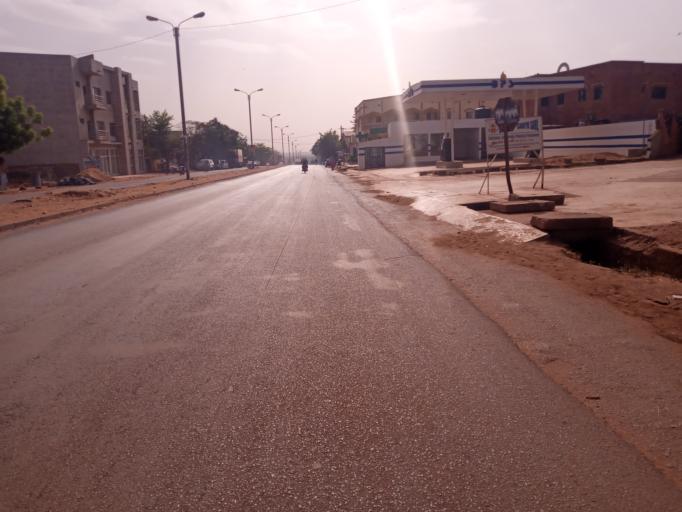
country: ML
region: Bamako
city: Bamako
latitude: 12.5767
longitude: -7.9520
